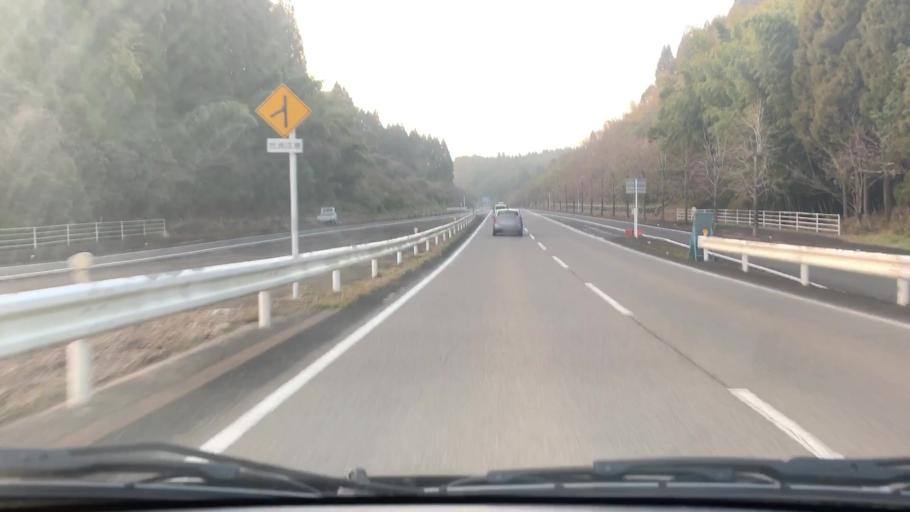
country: JP
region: Saga Prefecture
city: Imaricho-ko
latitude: 33.2648
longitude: 129.9586
